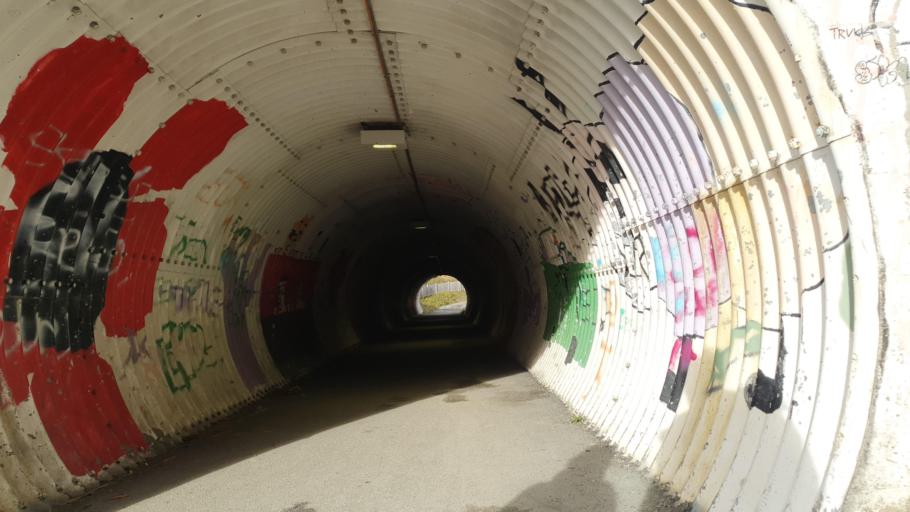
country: NO
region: Sor-Trondelag
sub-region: Klaebu
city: Klaebu
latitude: 63.3038
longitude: 10.4621
